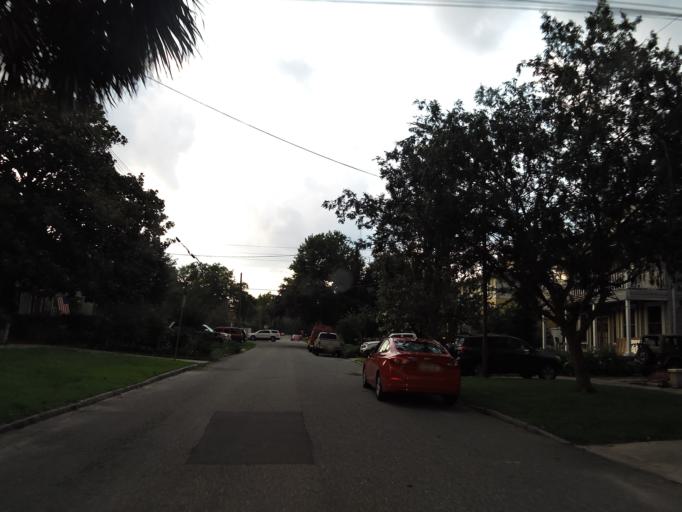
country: US
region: Florida
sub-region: Duval County
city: Jacksonville
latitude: 30.3120
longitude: -81.6865
